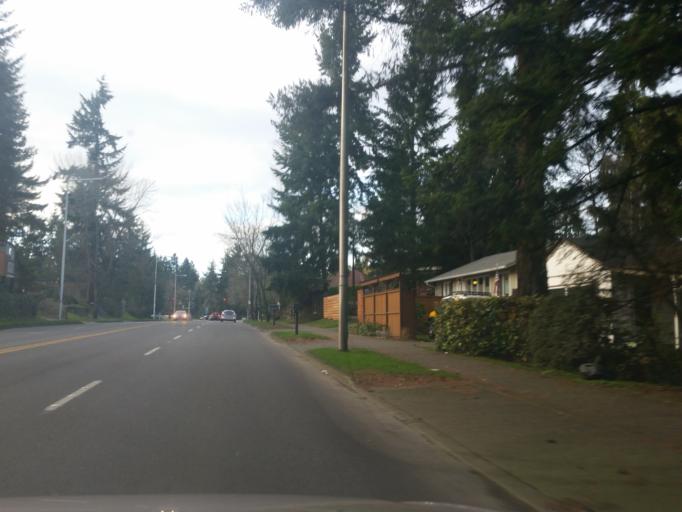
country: US
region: Washington
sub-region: King County
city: Shoreline
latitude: 47.7219
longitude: -122.3214
